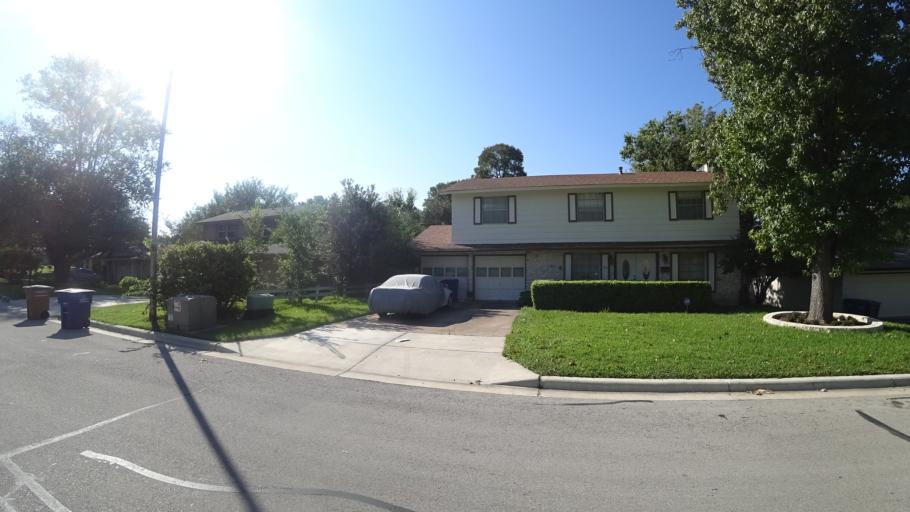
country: US
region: Texas
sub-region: Travis County
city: Austin
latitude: 30.3198
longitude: -97.6683
